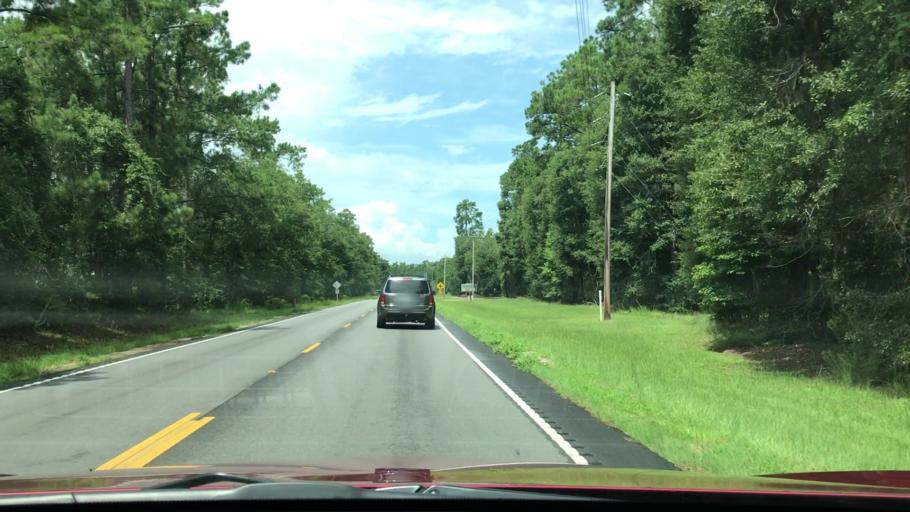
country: US
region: South Carolina
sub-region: Horry County
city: Red Hill
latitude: 33.9032
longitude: -78.9038
